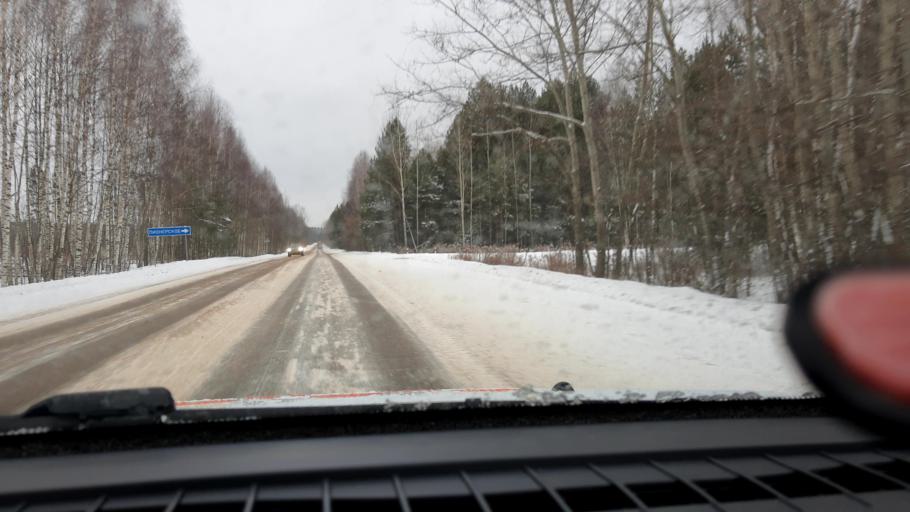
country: RU
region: Nizjnij Novgorod
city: Pamyat' Parizhskoy Kommuny
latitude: 56.2731
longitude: 44.4075
